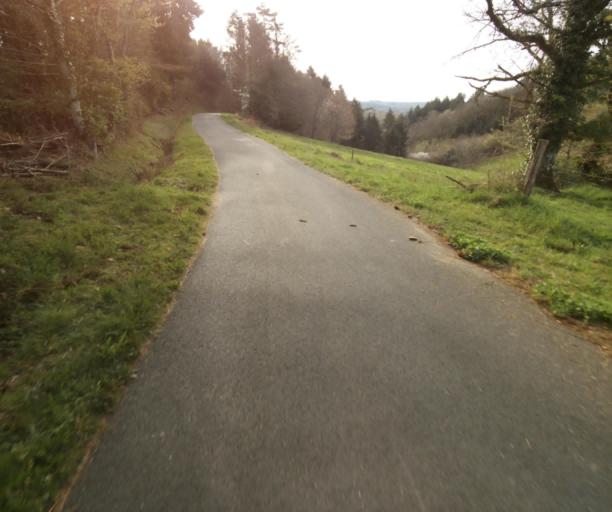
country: FR
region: Limousin
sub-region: Departement de la Correze
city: Chamboulive
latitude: 45.4359
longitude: 1.7844
